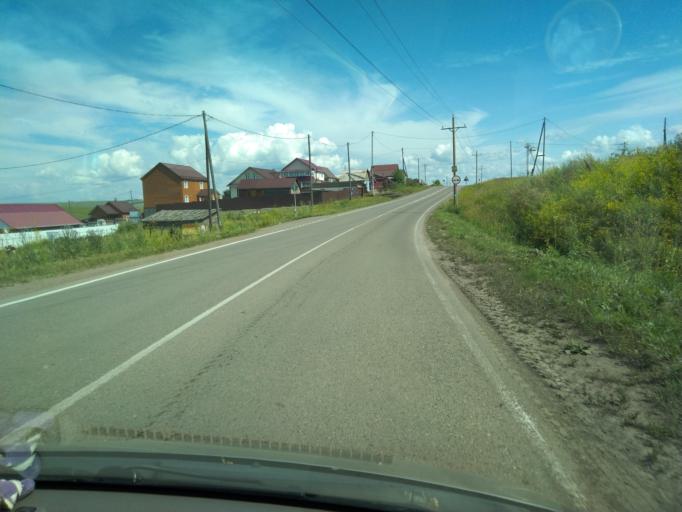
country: RU
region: Krasnoyarskiy
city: Zykovo
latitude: 55.9515
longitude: 93.1366
